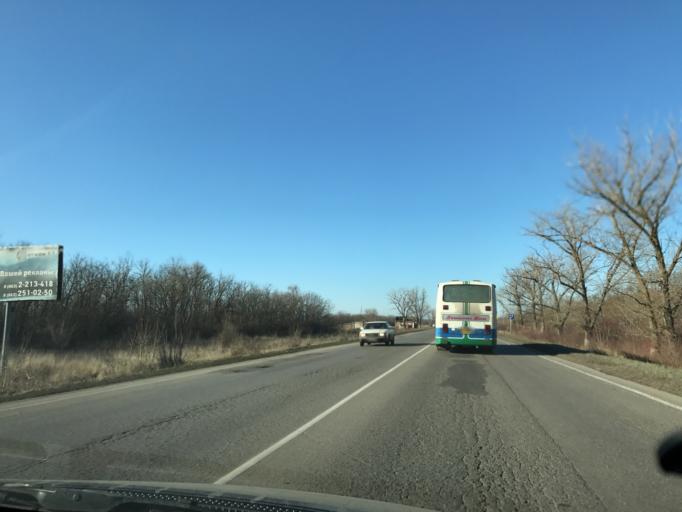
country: RU
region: Rostov
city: Kirovskaya
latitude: 47.0132
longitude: 39.9263
